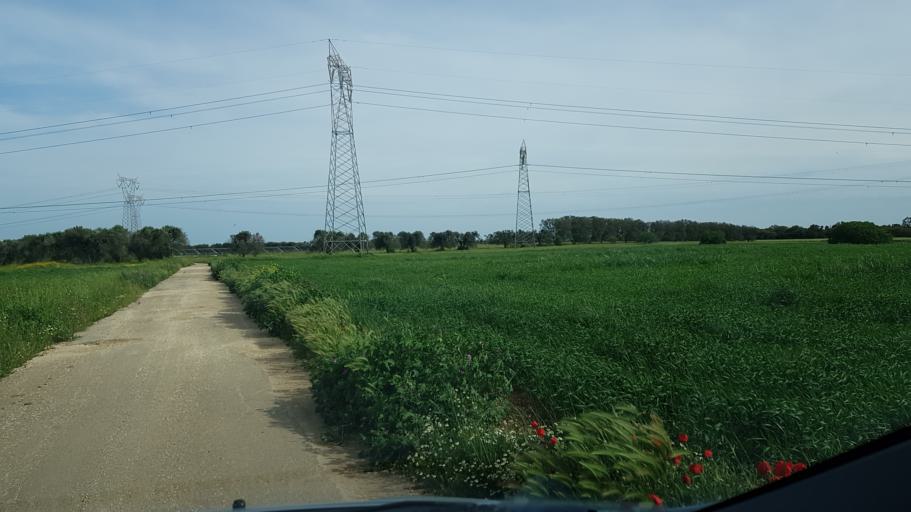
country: IT
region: Apulia
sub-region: Provincia di Brindisi
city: Tuturano
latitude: 40.5552
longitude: 17.9265
